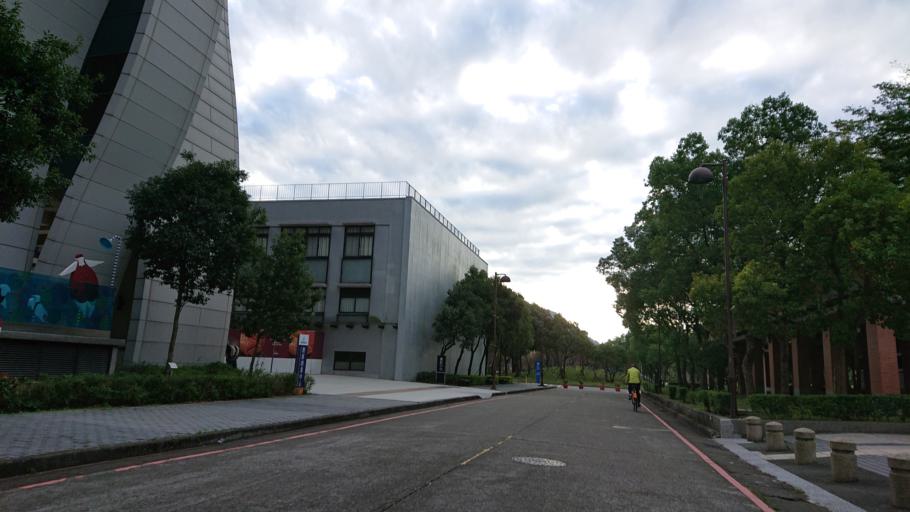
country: TW
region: Taiwan
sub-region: Taoyuan
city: Taoyuan
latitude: 24.9439
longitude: 121.3701
